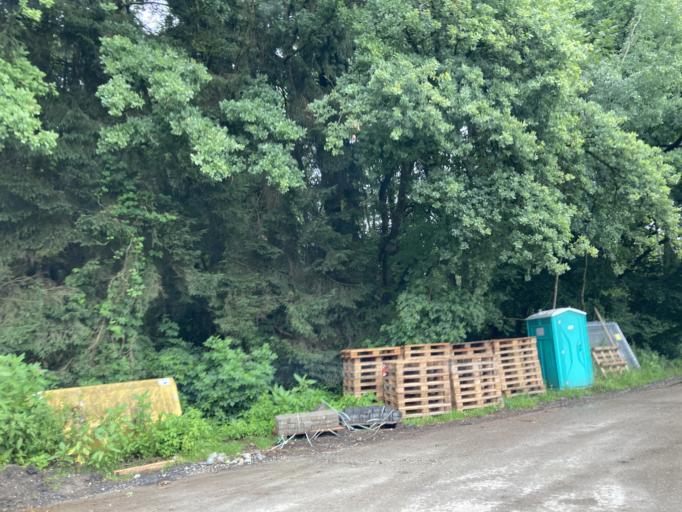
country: DE
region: Bavaria
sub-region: Upper Bavaria
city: Stephanskirchen
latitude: 47.8832
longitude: 12.1588
